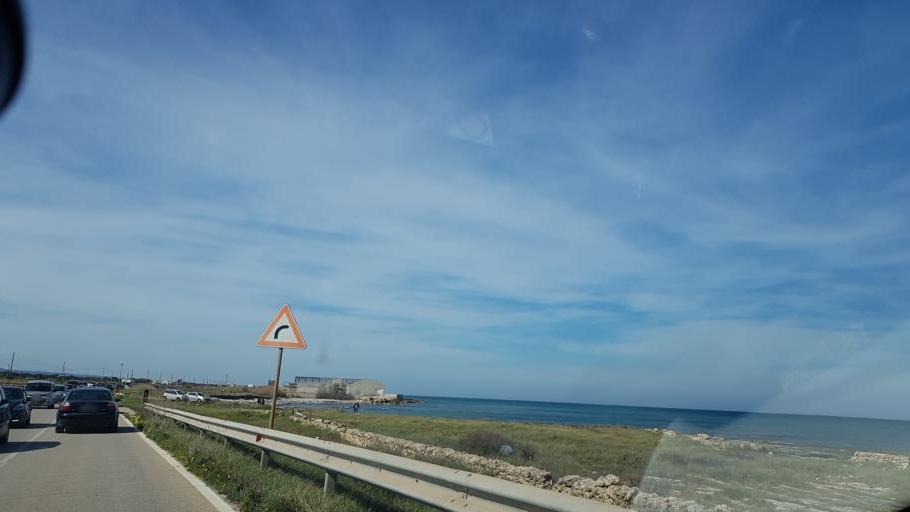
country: IT
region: Apulia
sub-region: Provincia di Brindisi
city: Pezze di Greco
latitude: 40.8581
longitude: 17.4344
